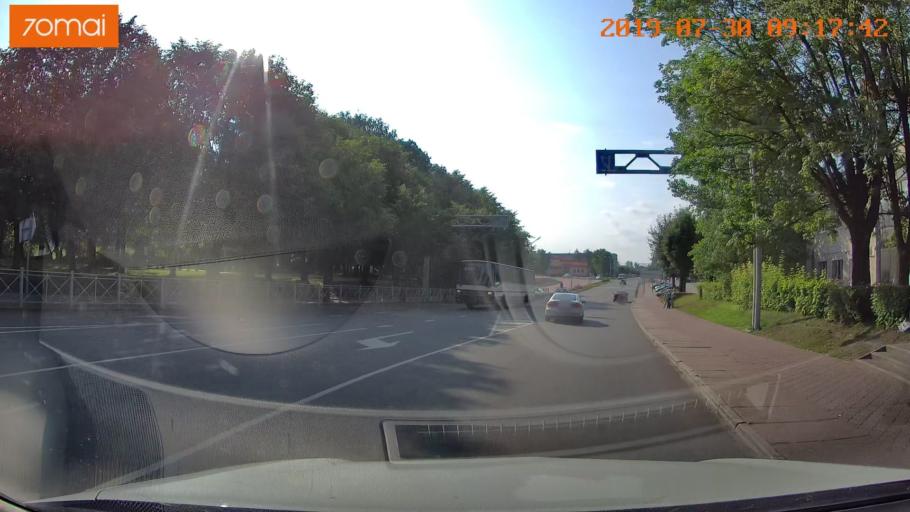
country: RU
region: Kaliningrad
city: Nesterov
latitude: 54.6327
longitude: 22.5697
